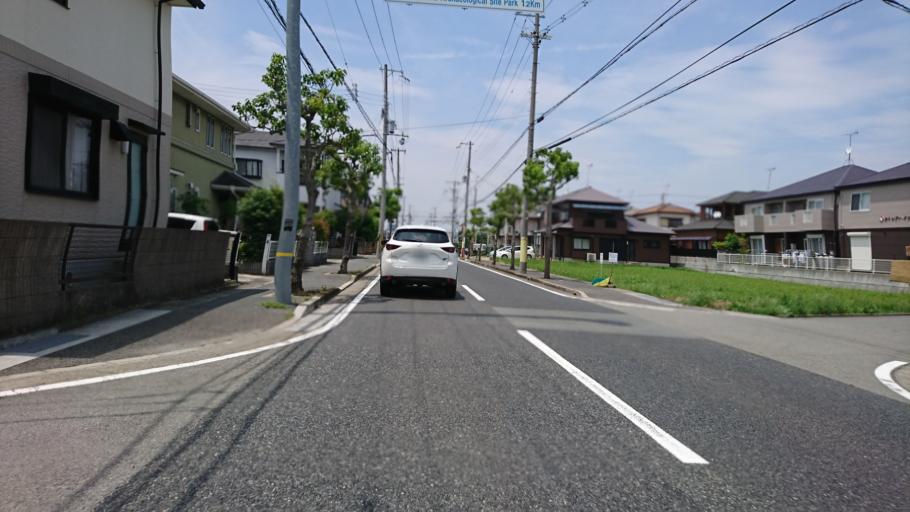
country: JP
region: Hyogo
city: Kakogawacho-honmachi
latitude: 34.7174
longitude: 134.8834
